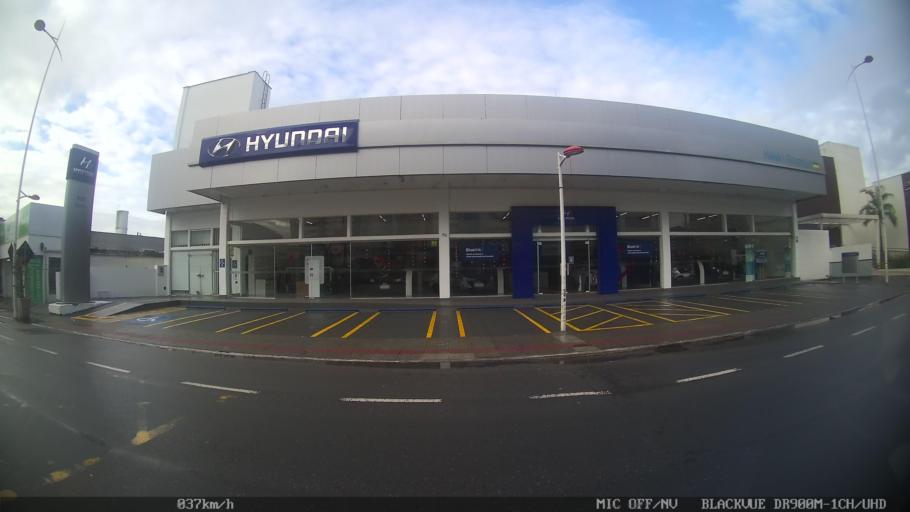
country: BR
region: Santa Catarina
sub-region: Sao Jose
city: Campinas
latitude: -27.6003
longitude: -48.6070
